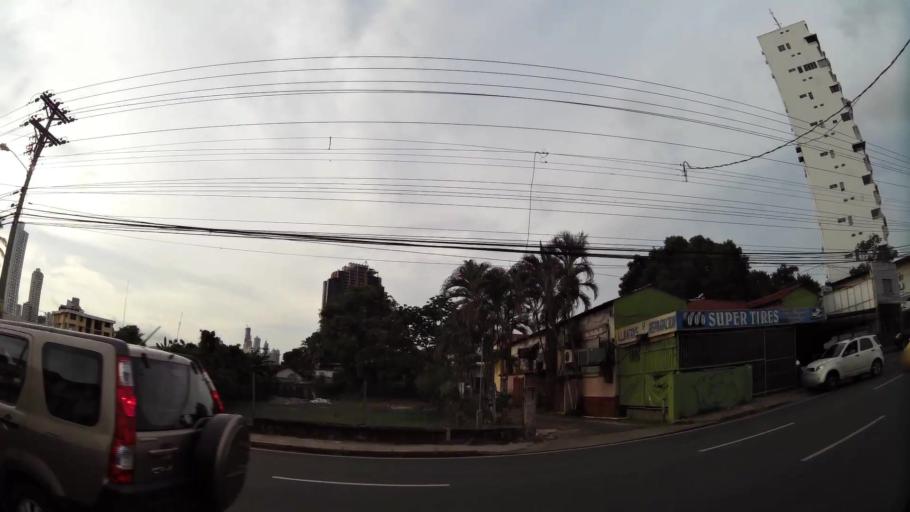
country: PA
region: Panama
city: Panama
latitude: 8.9943
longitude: -79.5156
